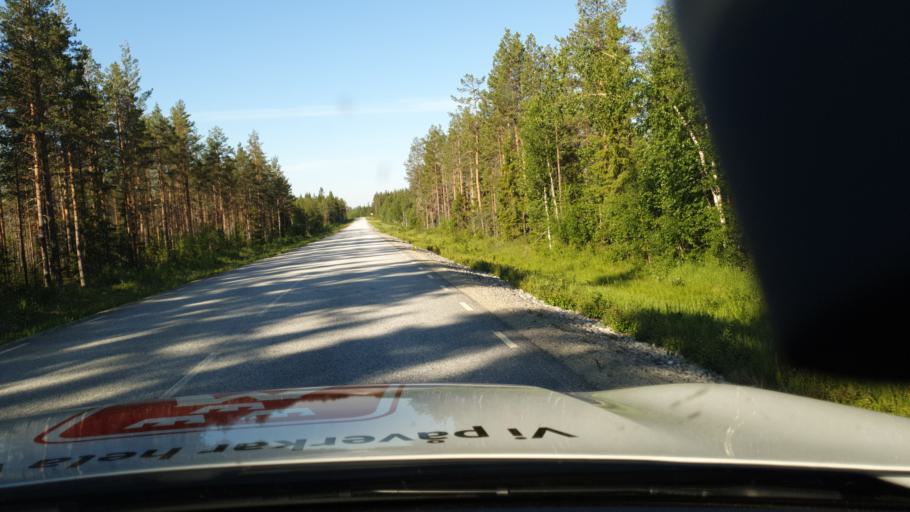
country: SE
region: Vaesterbotten
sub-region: Bjurholms Kommun
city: Bjurholm
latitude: 64.1582
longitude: 19.3648
